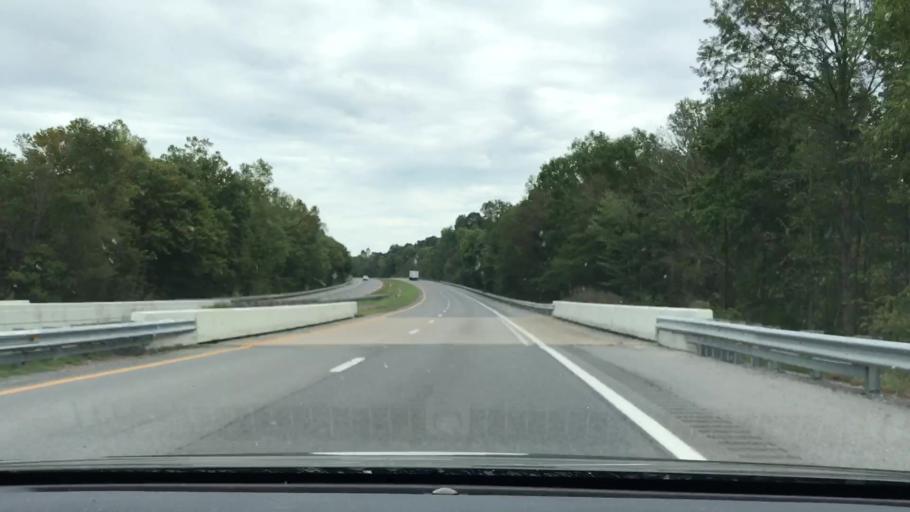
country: US
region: Kentucky
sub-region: Graves County
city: Mayfield
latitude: 36.7899
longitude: -88.5241
